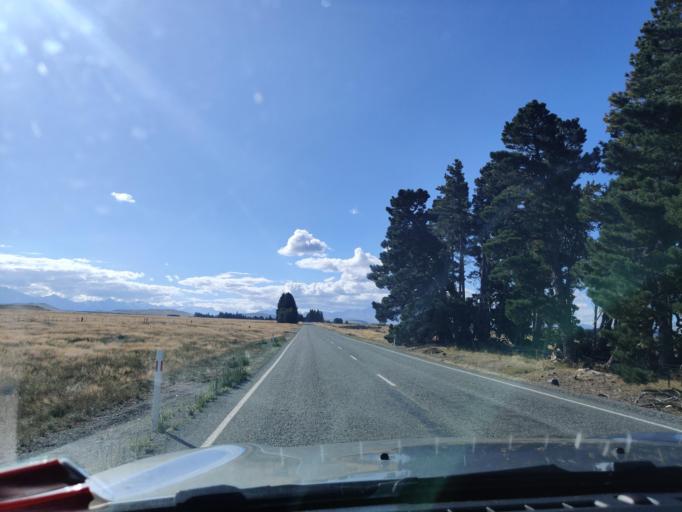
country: NZ
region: Canterbury
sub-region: Timaru District
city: Pleasant Point
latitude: -44.0988
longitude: 170.3539
